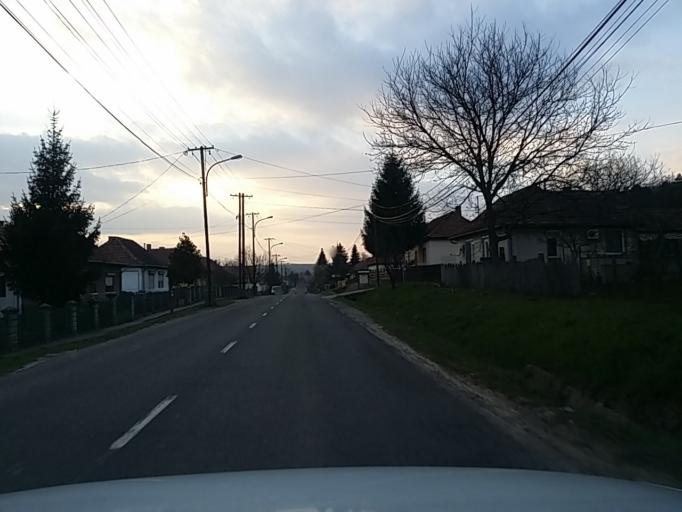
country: HU
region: Nograd
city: Matraterenye
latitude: 48.0030
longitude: 19.9150
